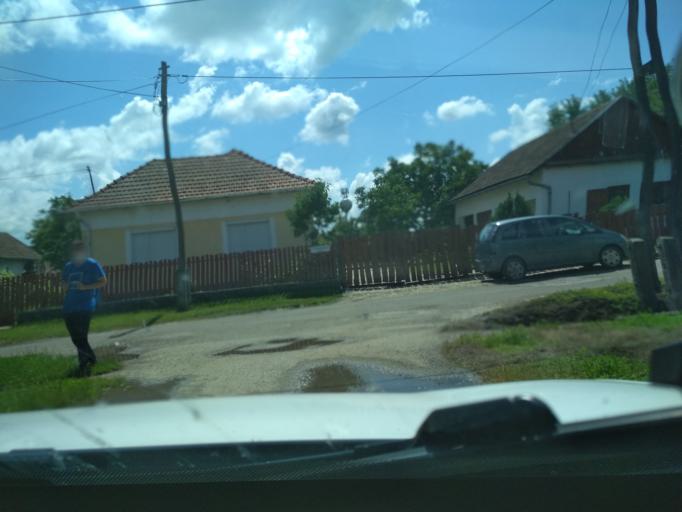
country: HU
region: Jasz-Nagykun-Szolnok
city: Abadszalok
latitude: 47.4790
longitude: 20.5992
